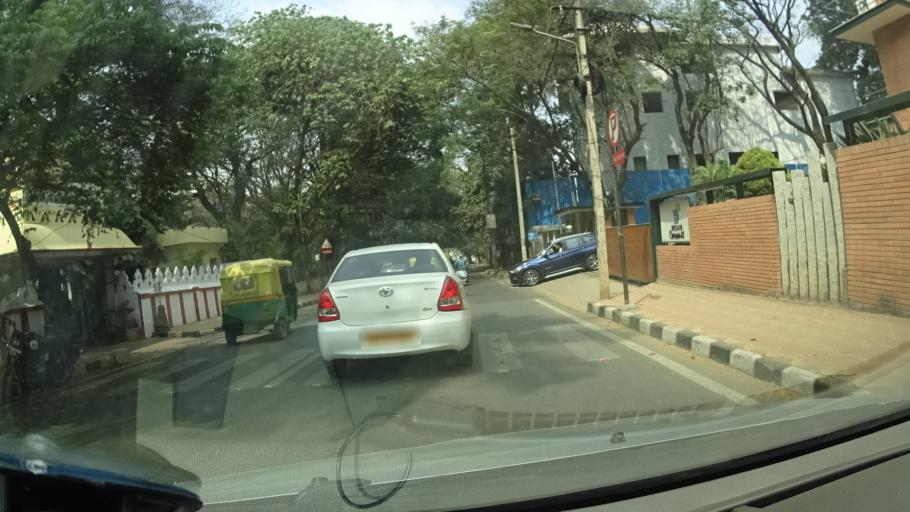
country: IN
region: Karnataka
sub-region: Bangalore Urban
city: Bangalore
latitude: 12.9887
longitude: 77.5888
